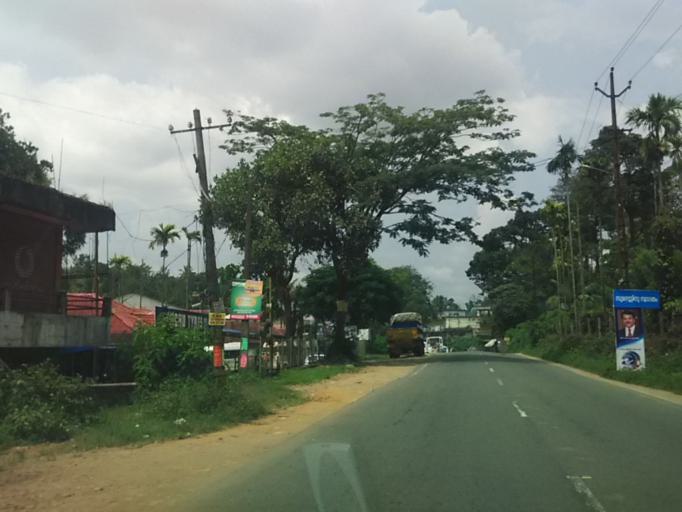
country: IN
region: Kerala
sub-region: Wayanad
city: Kalpetta
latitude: 11.6021
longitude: 76.0832
